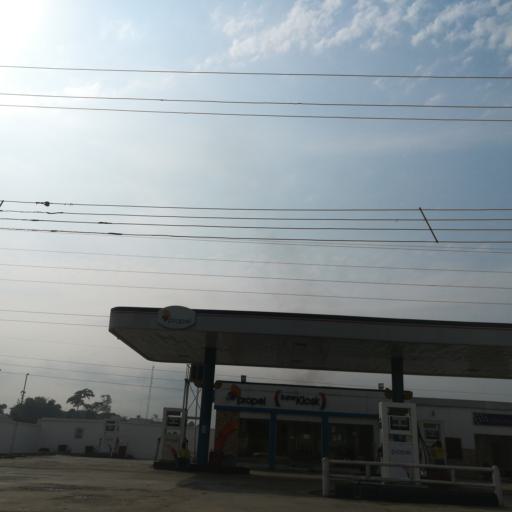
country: NG
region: Rivers
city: Port Harcourt
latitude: 4.8513
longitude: 7.0599
